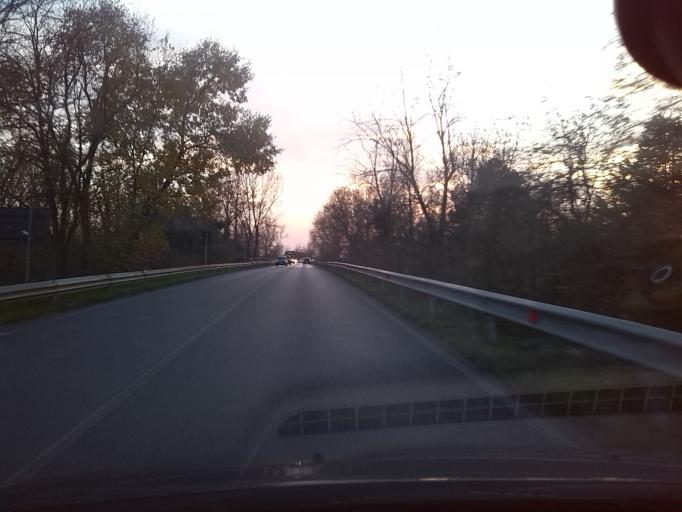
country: IT
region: Friuli Venezia Giulia
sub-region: Provincia di Udine
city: Pradamano
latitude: 46.0441
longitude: 13.3114
